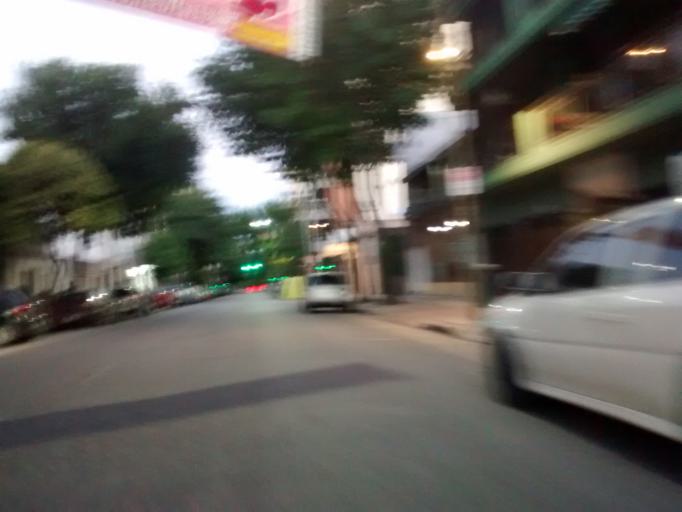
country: AR
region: Buenos Aires F.D.
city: Villa Santa Rita
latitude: -34.6118
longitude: -58.4516
